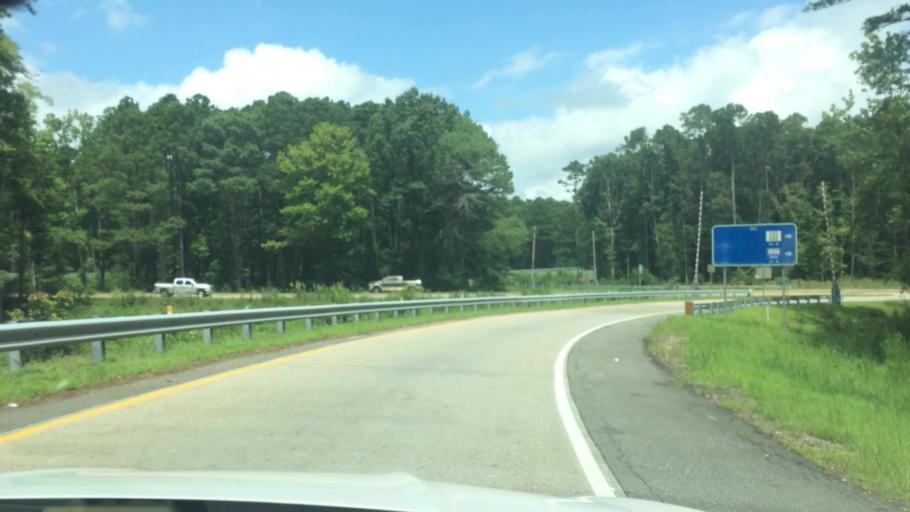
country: US
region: Virginia
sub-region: York County
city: Yorktown
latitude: 37.1736
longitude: -76.5533
